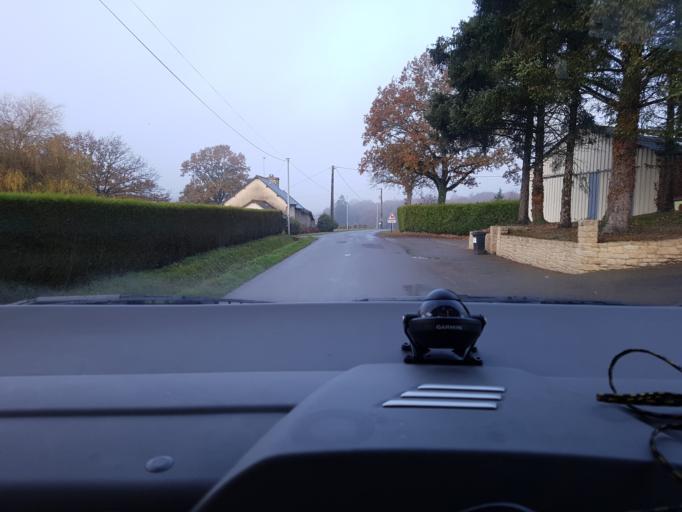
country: FR
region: Brittany
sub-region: Departement d'Ille-et-Vilaine
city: Livre-sur-Changeon
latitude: 48.1879
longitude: -1.3460
